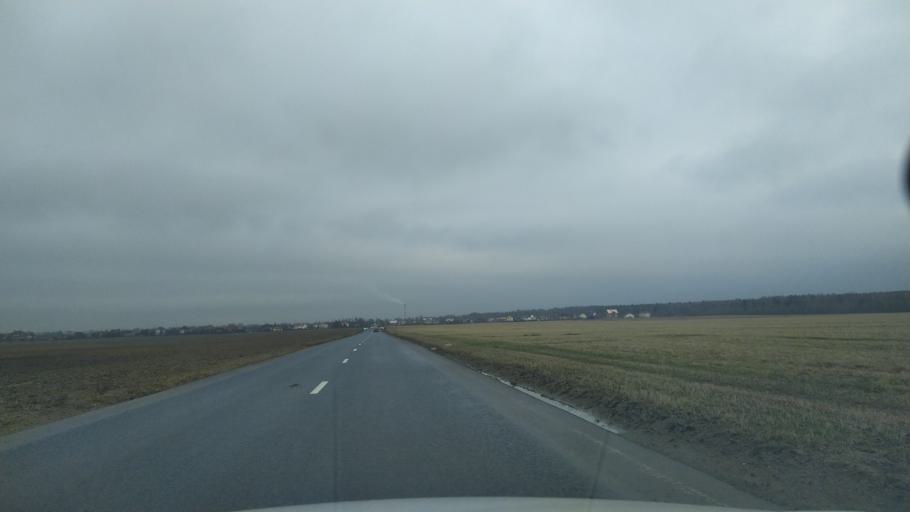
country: RU
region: St.-Petersburg
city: Aleksandrovskaya
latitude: 59.7151
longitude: 30.3356
